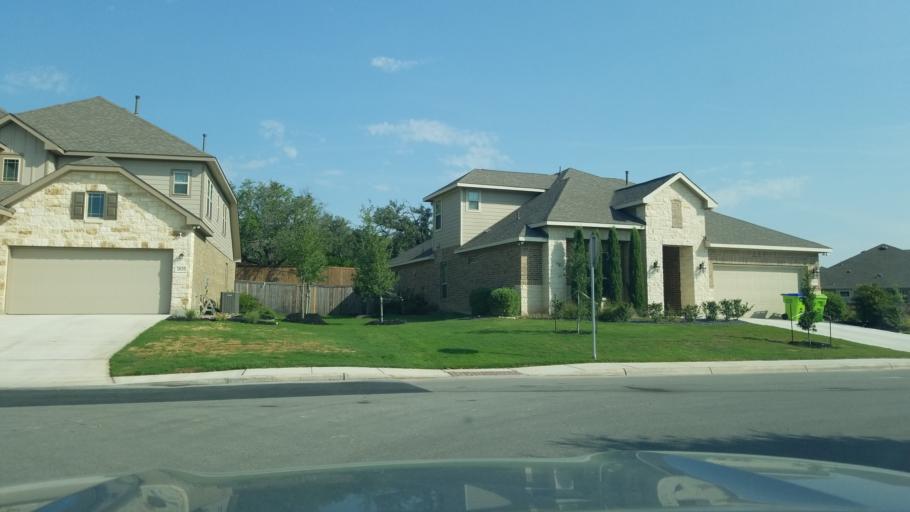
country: US
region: Texas
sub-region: Medina County
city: La Coste
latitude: 29.4017
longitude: -98.7804
